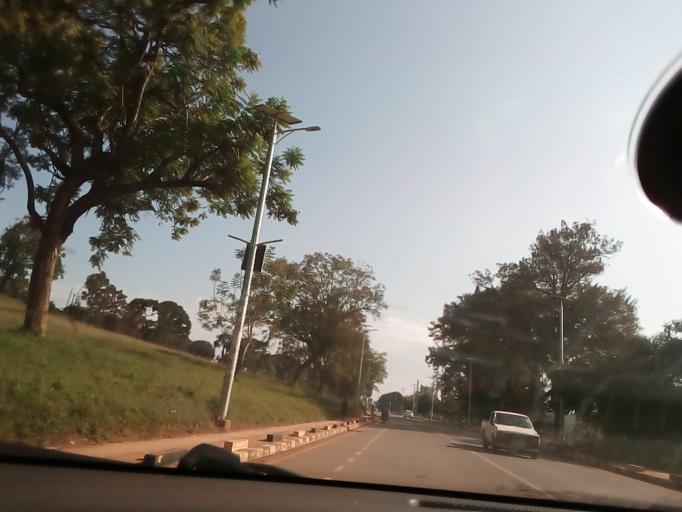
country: UG
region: Central Region
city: Masaka
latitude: -0.3353
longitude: 31.7380
